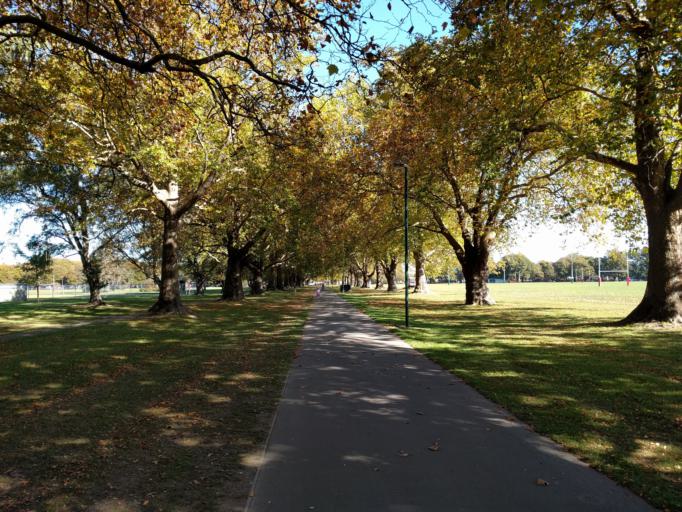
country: NZ
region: Canterbury
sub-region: Christchurch City
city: Christchurch
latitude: -43.5275
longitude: 172.6176
